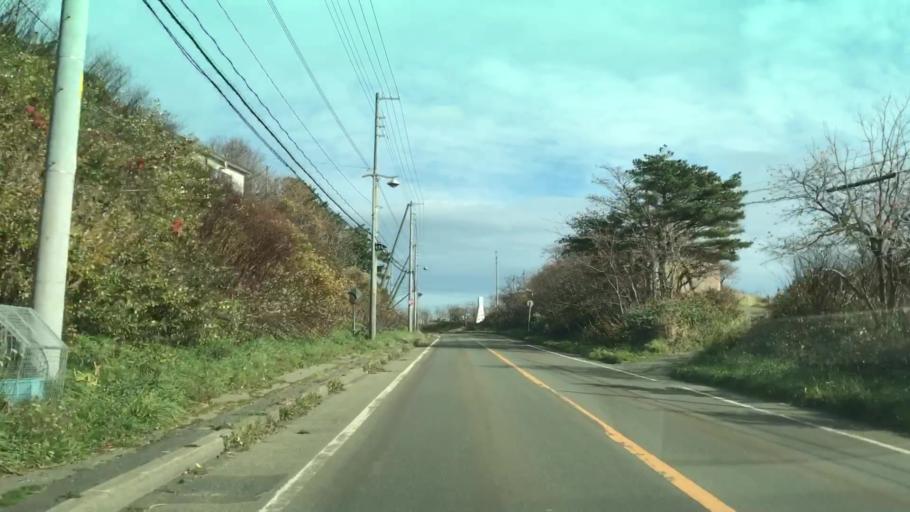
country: JP
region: Hokkaido
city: Obihiro
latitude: 42.0445
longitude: 143.2971
